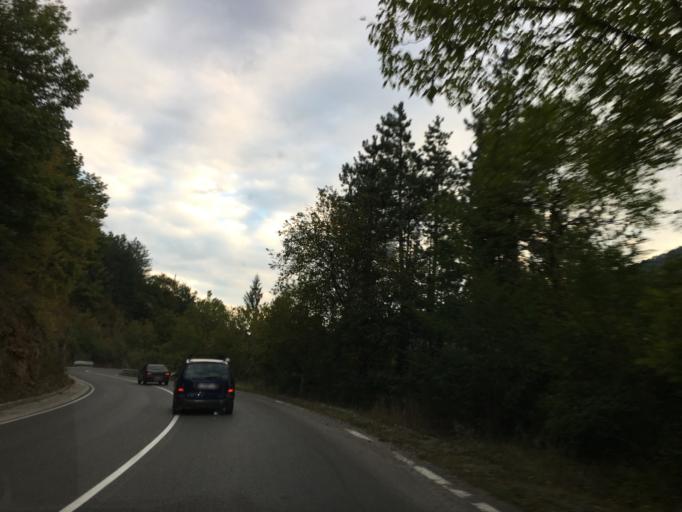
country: BG
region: Sofiya
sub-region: Obshtina Svoge
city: Svoge
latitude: 42.9405
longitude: 23.3829
